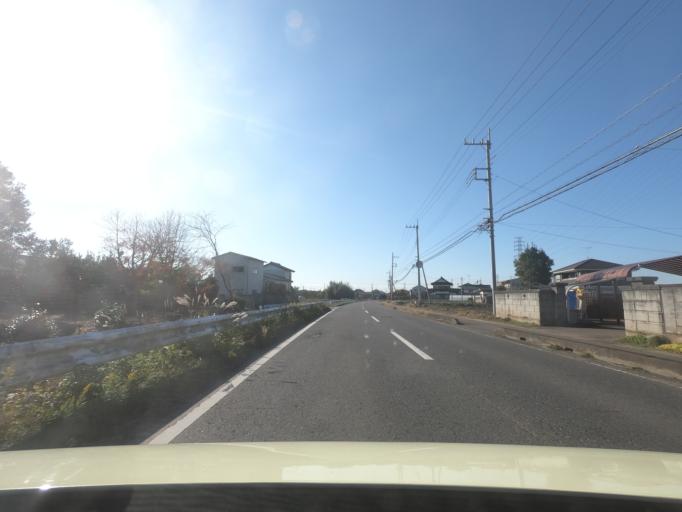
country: JP
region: Ibaraki
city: Ishige
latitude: 36.1735
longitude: 139.9842
